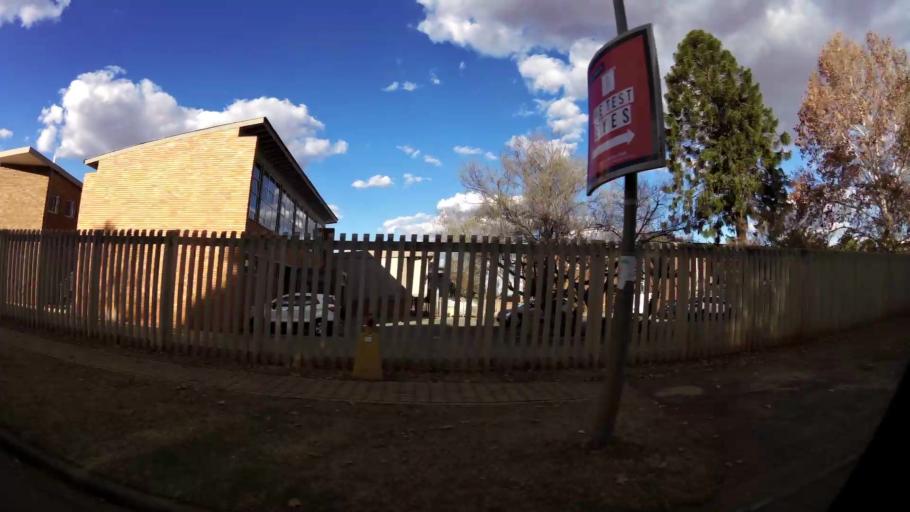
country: ZA
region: North-West
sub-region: Dr Kenneth Kaunda District Municipality
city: Potchefstroom
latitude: -26.6905
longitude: 27.0982
